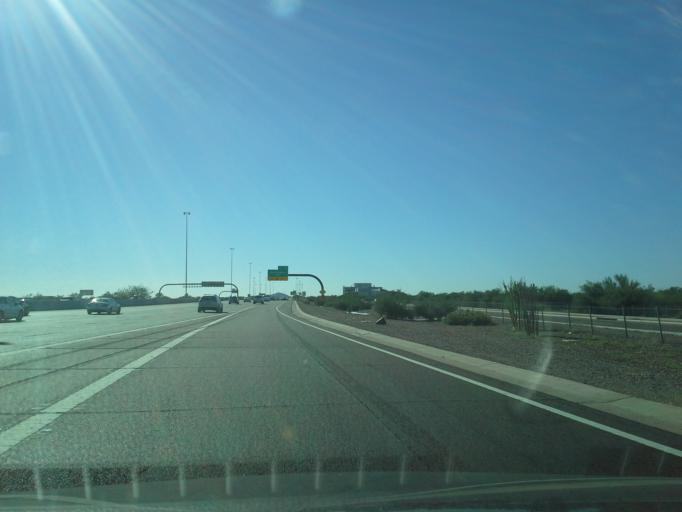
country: US
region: Arizona
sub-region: Maricopa County
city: Paradise Valley
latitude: 33.6558
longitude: -111.9129
